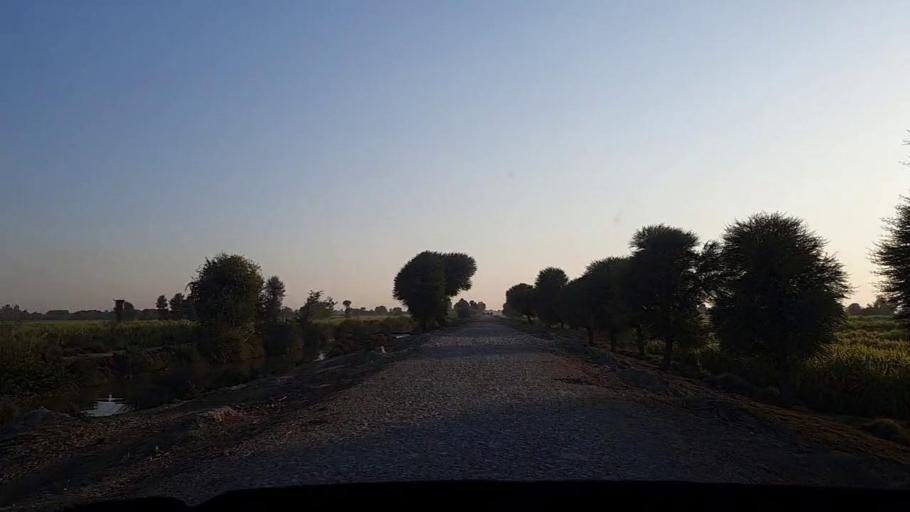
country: PK
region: Sindh
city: Sobhadero
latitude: 27.3750
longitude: 68.3791
